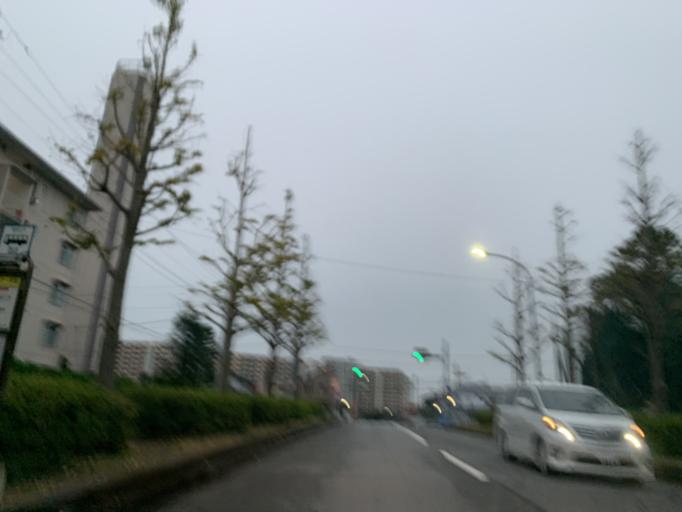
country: JP
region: Chiba
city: Funabashi
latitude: 35.6626
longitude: 140.0377
